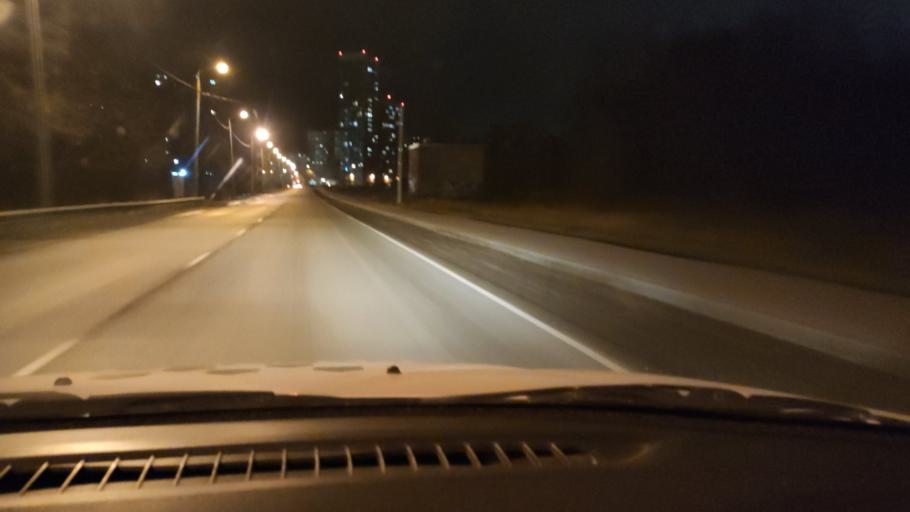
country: RU
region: Perm
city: Kondratovo
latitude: 57.9883
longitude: 56.1346
